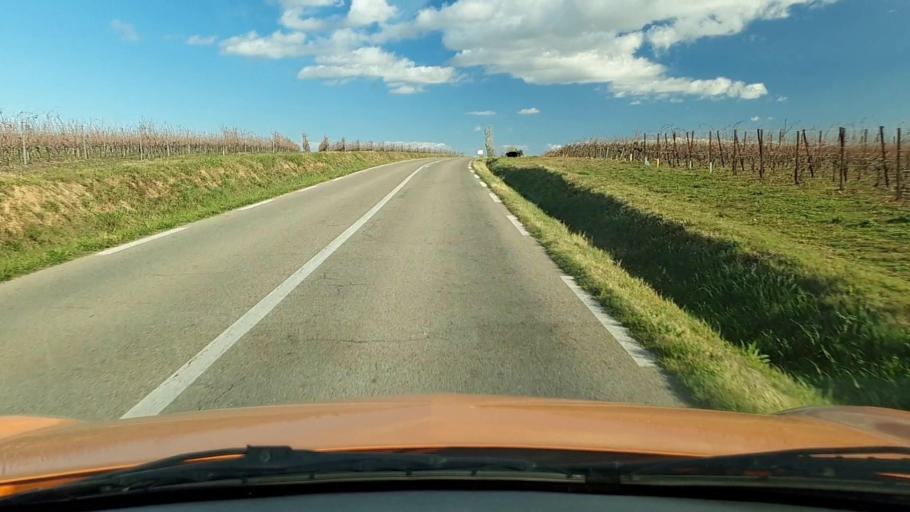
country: FR
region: Languedoc-Roussillon
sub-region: Departement du Gard
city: Vauvert
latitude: 43.6522
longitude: 4.3076
